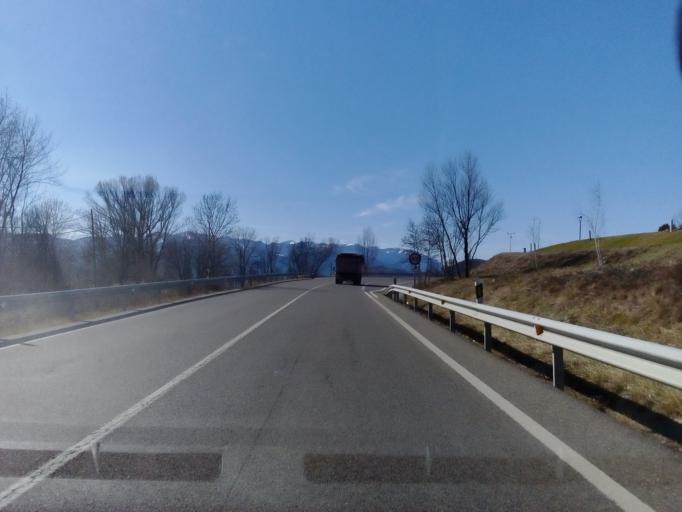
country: ES
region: Catalonia
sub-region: Provincia de Girona
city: Bolvir
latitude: 42.4164
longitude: 1.8781
